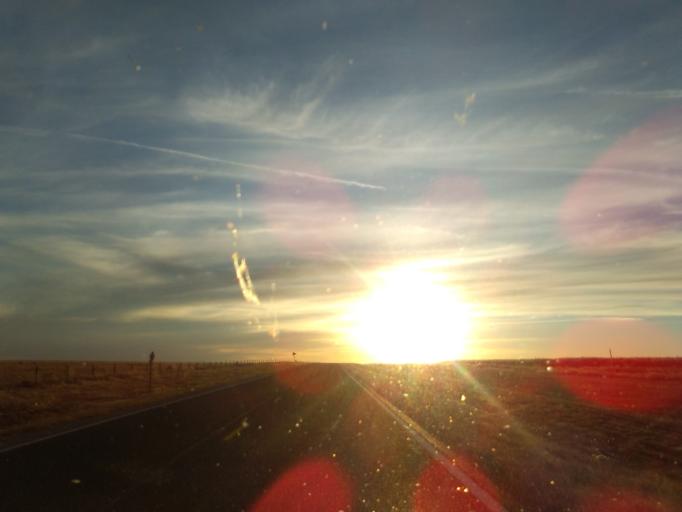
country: US
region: Kansas
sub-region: Wallace County
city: Sharon Springs
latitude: 38.9857
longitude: -101.4199
